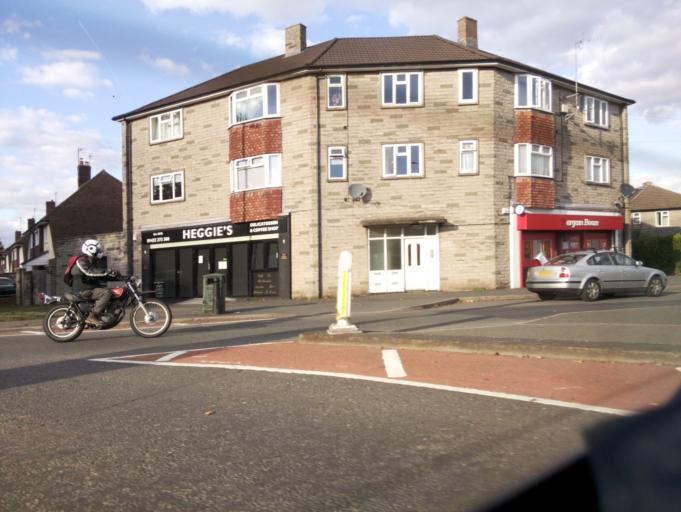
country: GB
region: England
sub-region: Herefordshire
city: Belmont
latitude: 52.0621
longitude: -2.7407
